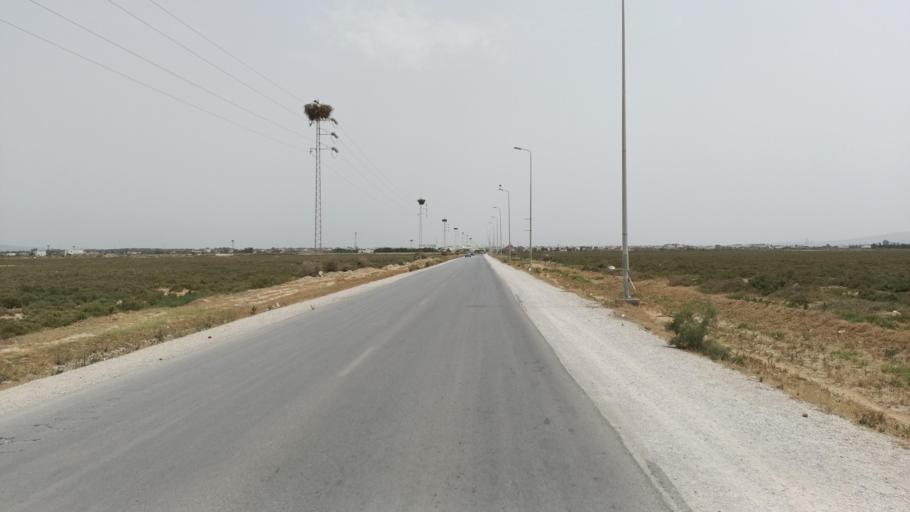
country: TN
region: Nabul
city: Manzil Bu Zalafah
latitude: 36.7190
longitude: 10.4758
